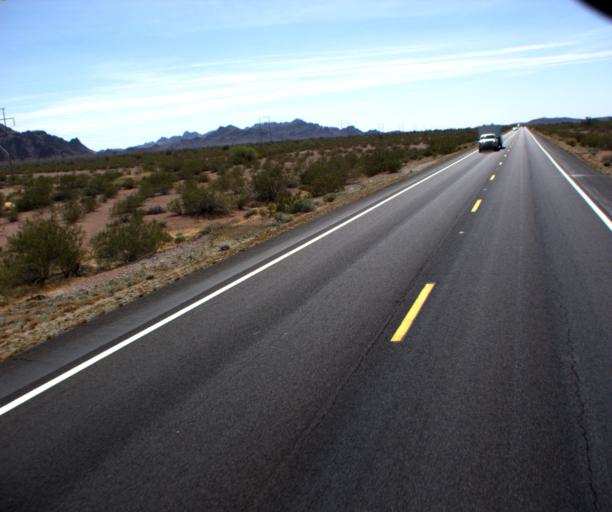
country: US
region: Arizona
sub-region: La Paz County
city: Quartzsite
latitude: 33.2960
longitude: -114.2226
